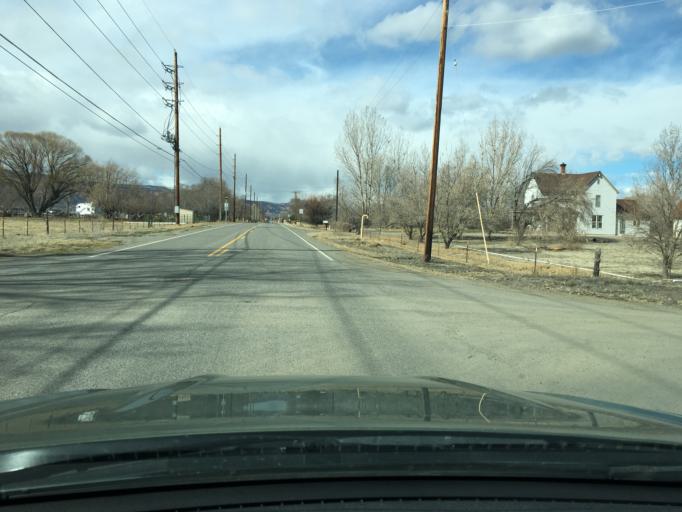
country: US
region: Colorado
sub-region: Mesa County
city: Redlands
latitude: 39.1209
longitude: -108.6173
